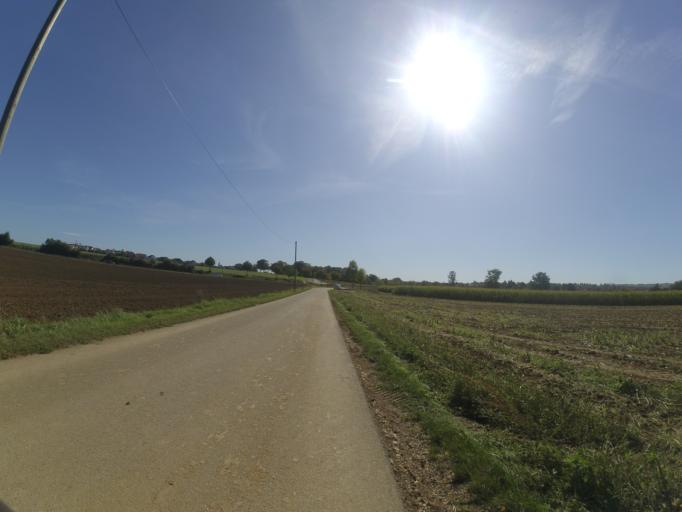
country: DE
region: Baden-Wuerttemberg
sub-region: Tuebingen Region
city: Langenau
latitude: 48.5020
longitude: 10.1009
